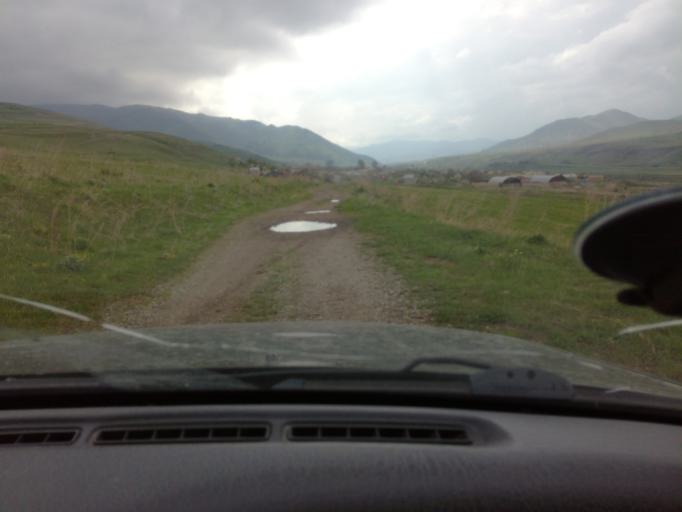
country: AM
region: Lorri
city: Lerrnapat
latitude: 40.8403
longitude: 44.3679
